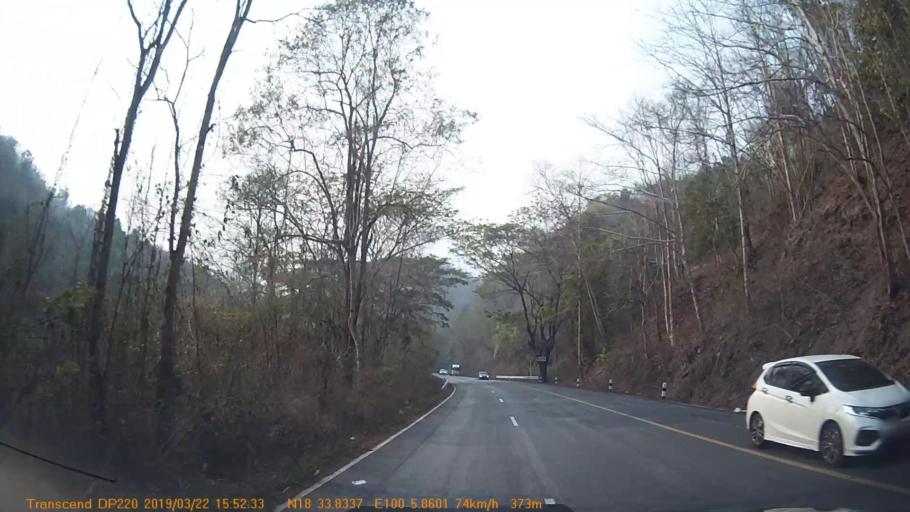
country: TH
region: Phrae
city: Song
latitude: 18.5642
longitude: 100.0974
